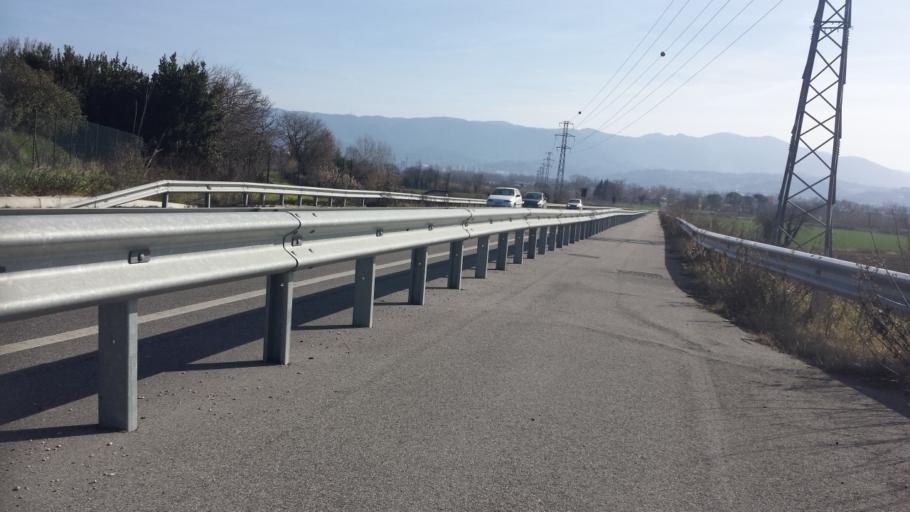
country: IT
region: Umbria
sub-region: Provincia di Terni
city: Terni
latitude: 42.5746
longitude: 12.5993
